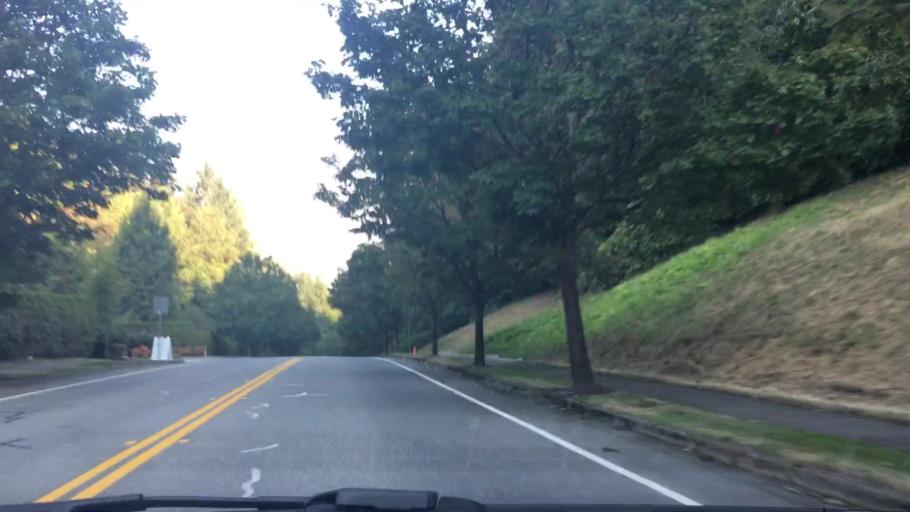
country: US
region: Washington
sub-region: King County
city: West Lake Sammamish
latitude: 47.5582
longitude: -122.0911
